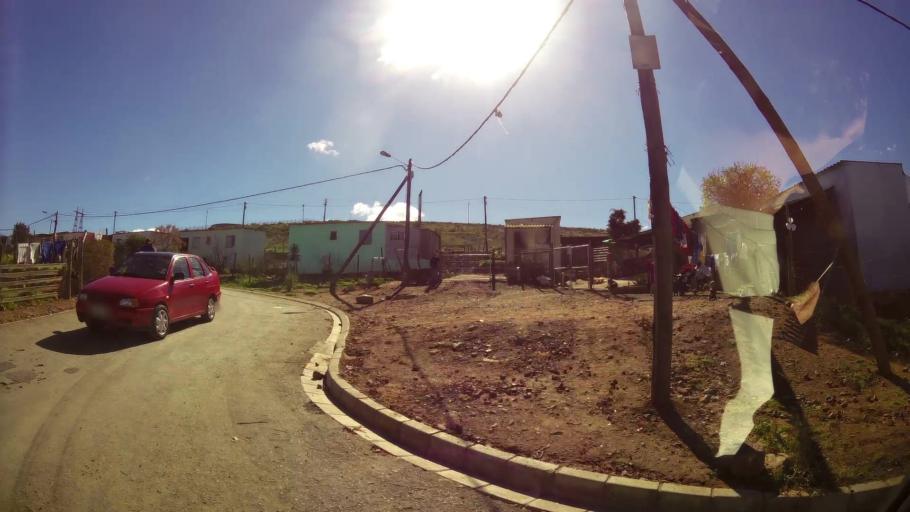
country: ZA
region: Western Cape
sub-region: Cape Winelands District Municipality
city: Ashton
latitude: -33.8301
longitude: 20.0471
